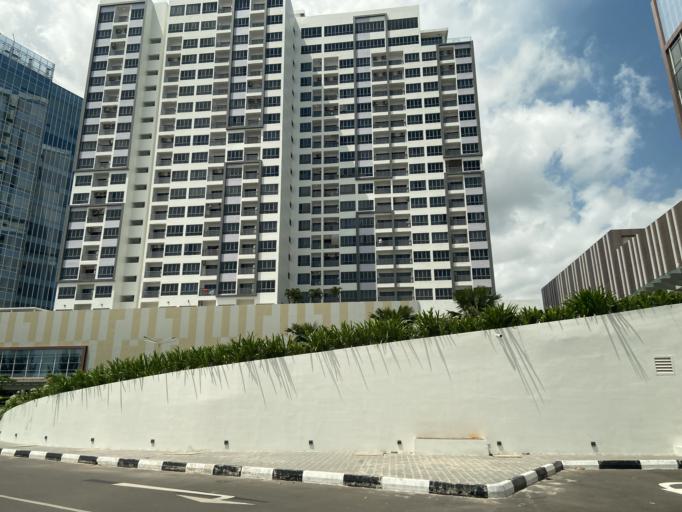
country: SG
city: Singapore
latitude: 1.1546
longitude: 103.9968
